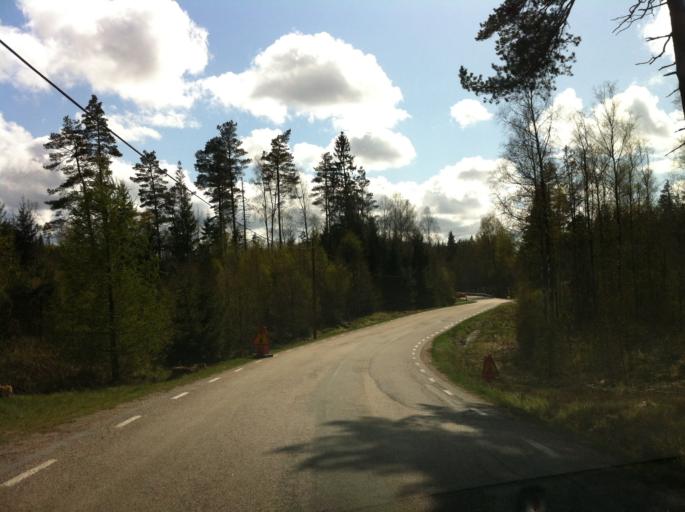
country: SE
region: Vaestra Goetaland
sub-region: Alingsas Kommun
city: Alingsas
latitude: 57.8338
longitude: 12.6509
